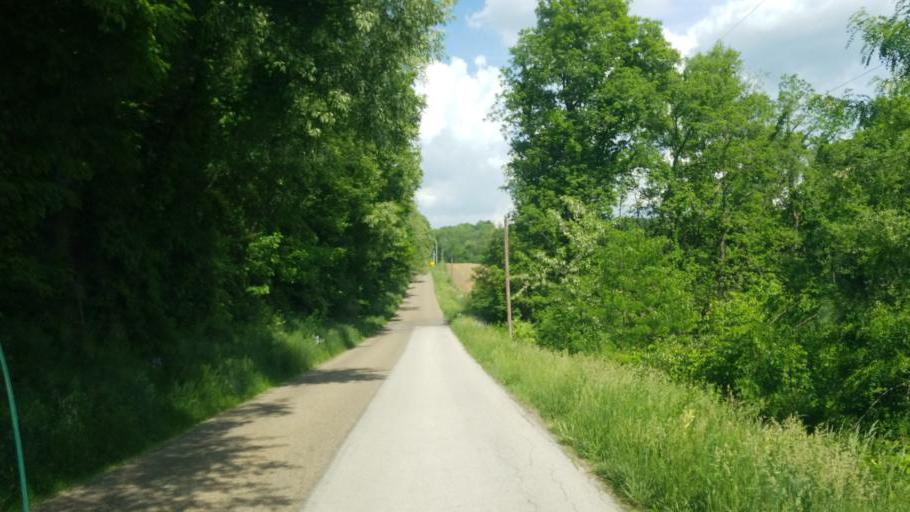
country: US
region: Ohio
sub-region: Sandusky County
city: Bellville
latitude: 40.6520
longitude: -82.5310
